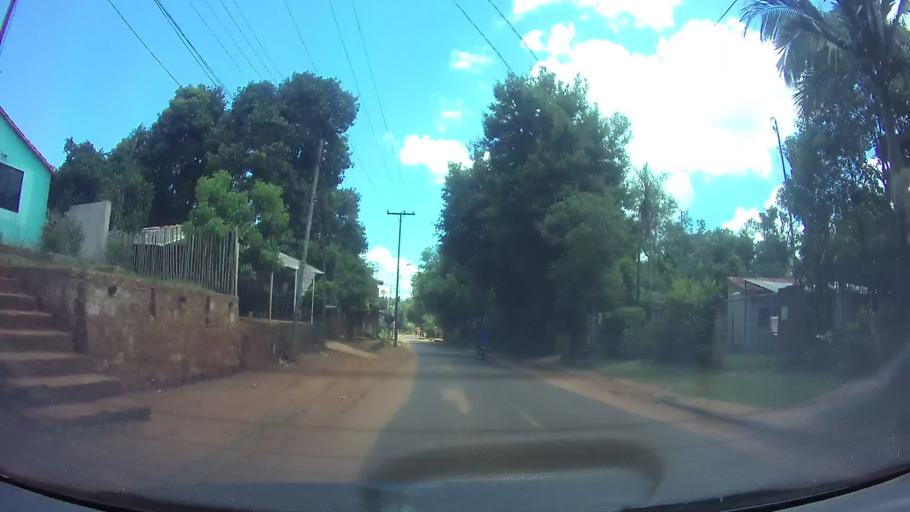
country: PY
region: Central
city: Itaugua
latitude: -25.3839
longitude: -57.3659
